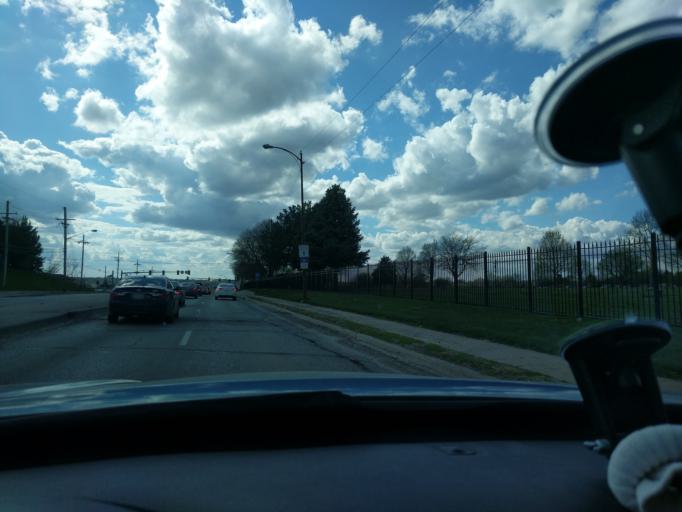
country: US
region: Nebraska
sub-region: Douglas County
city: Ralston
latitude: 41.2343
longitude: -96.0313
